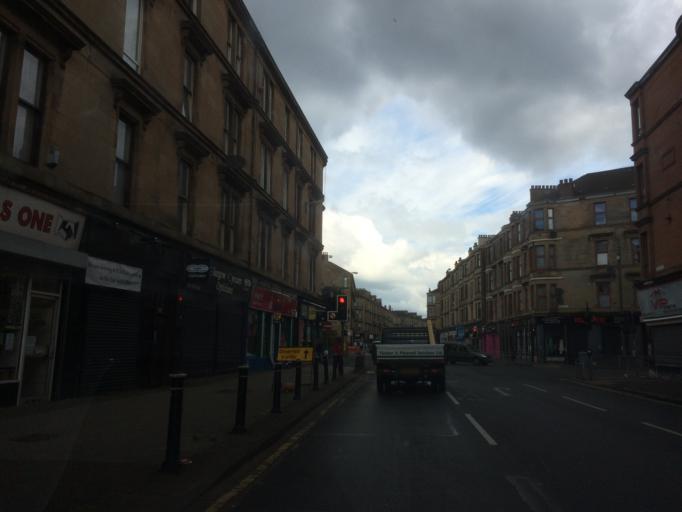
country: GB
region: Scotland
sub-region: Glasgow City
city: Glasgow
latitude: 55.8346
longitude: -4.2563
